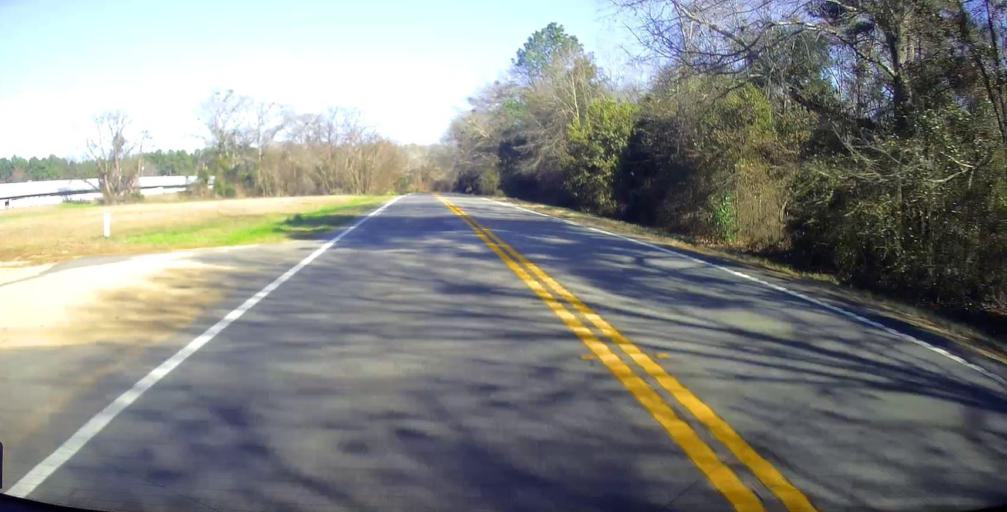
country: US
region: Georgia
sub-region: Macon County
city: Oglethorpe
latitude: 32.3516
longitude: -84.1599
